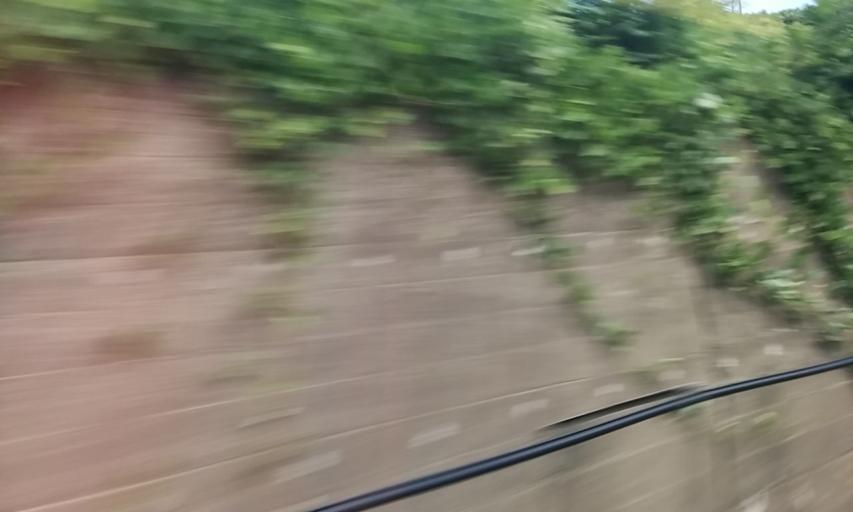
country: JP
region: Fukushima
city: Koriyama
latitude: 37.4341
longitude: 140.3999
